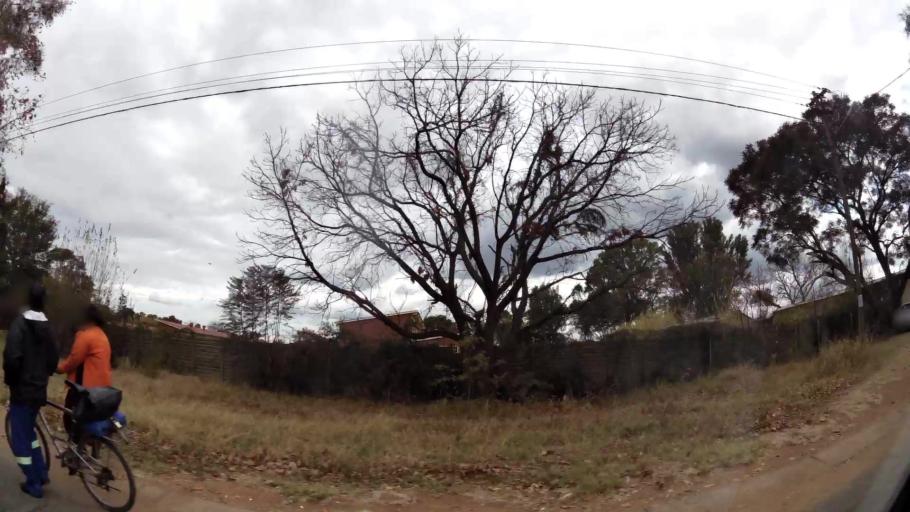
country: ZA
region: Limpopo
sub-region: Waterberg District Municipality
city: Modimolle
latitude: -24.7025
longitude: 28.4097
